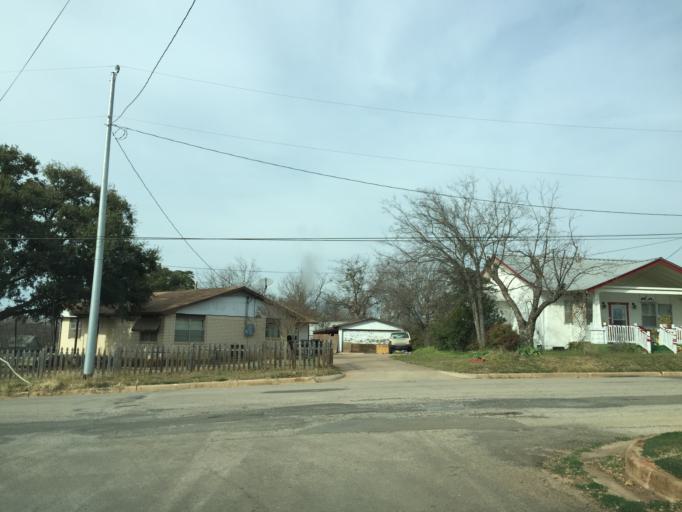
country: US
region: Texas
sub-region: Llano County
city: Llano
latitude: 30.7442
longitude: -98.6721
